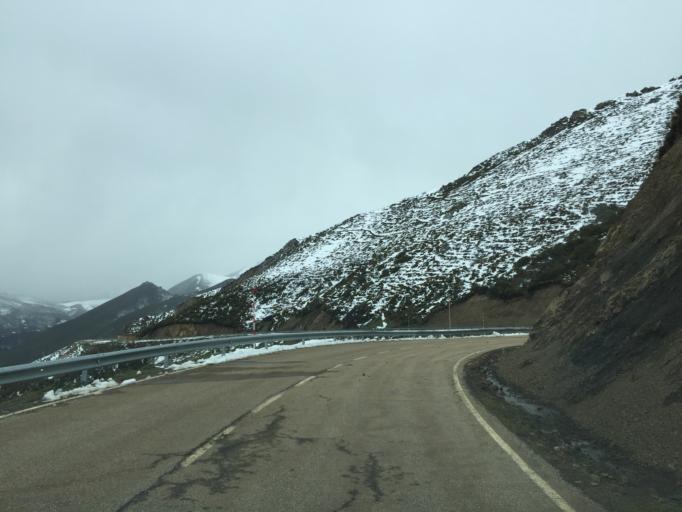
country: ES
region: Castille and Leon
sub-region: Provincia de Leon
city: San Emiliano
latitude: 43.0573
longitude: -6.0050
